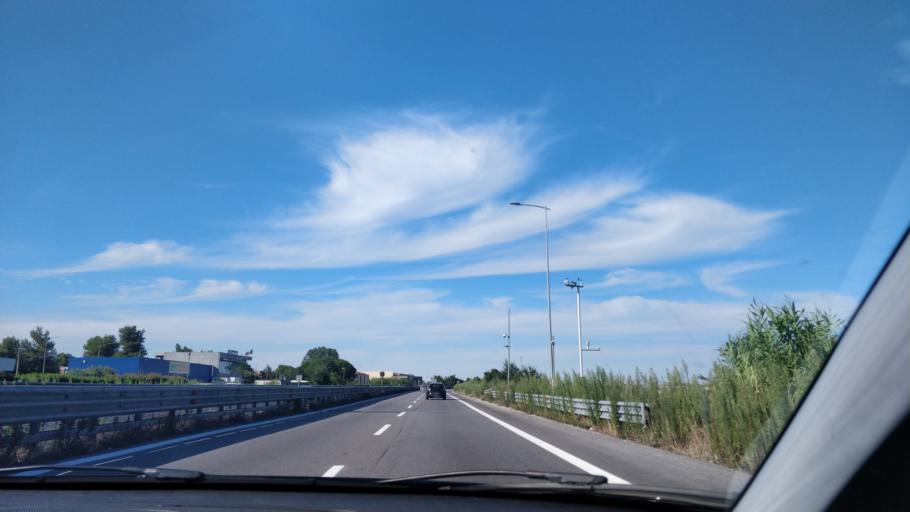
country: IT
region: Abruzzo
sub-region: Provincia di Pescara
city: Santa Teresa
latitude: 42.4209
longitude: 14.1697
